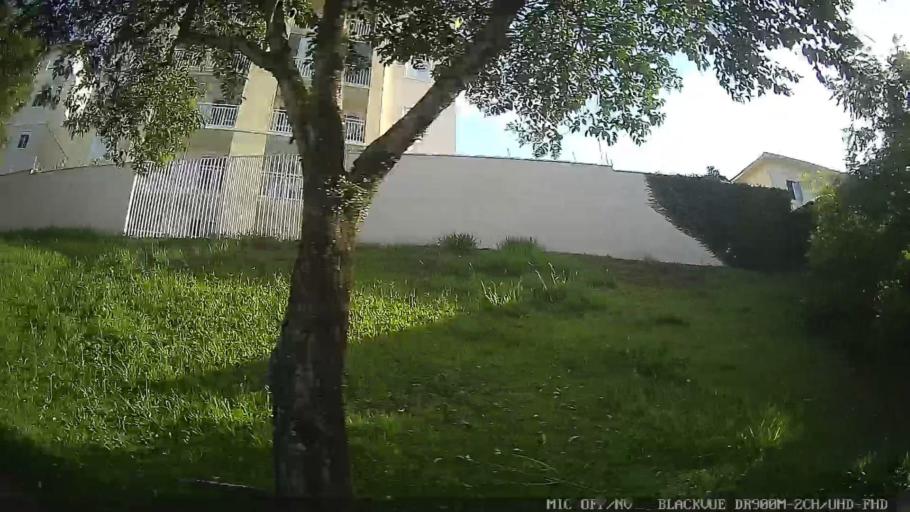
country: BR
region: Sao Paulo
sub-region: Mogi das Cruzes
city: Mogi das Cruzes
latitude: -23.5112
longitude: -46.1525
